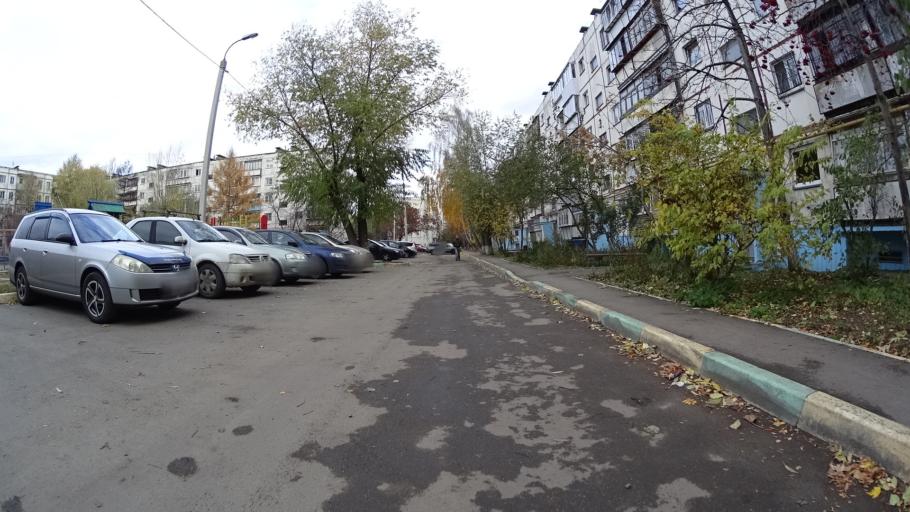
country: RU
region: Chelyabinsk
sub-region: Gorod Chelyabinsk
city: Chelyabinsk
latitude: 55.1897
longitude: 61.3142
